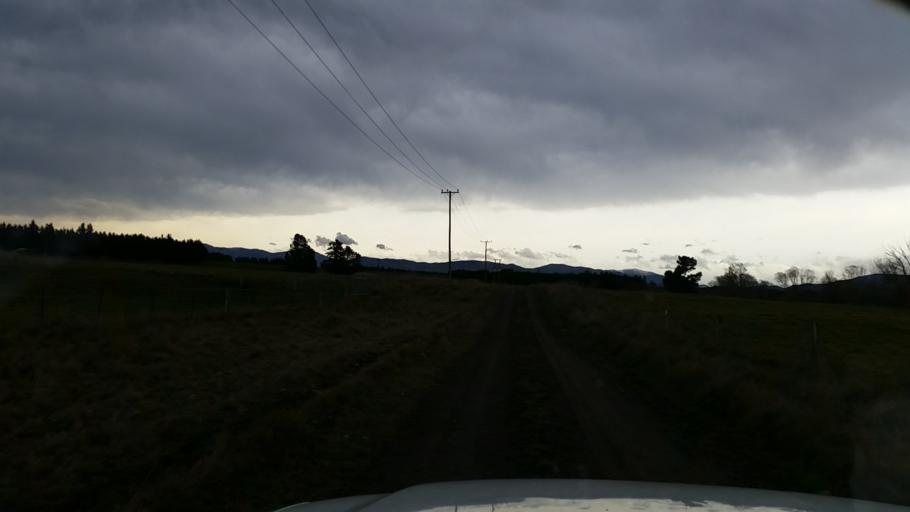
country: NZ
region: Canterbury
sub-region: Ashburton District
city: Methven
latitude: -43.6980
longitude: 171.4806
